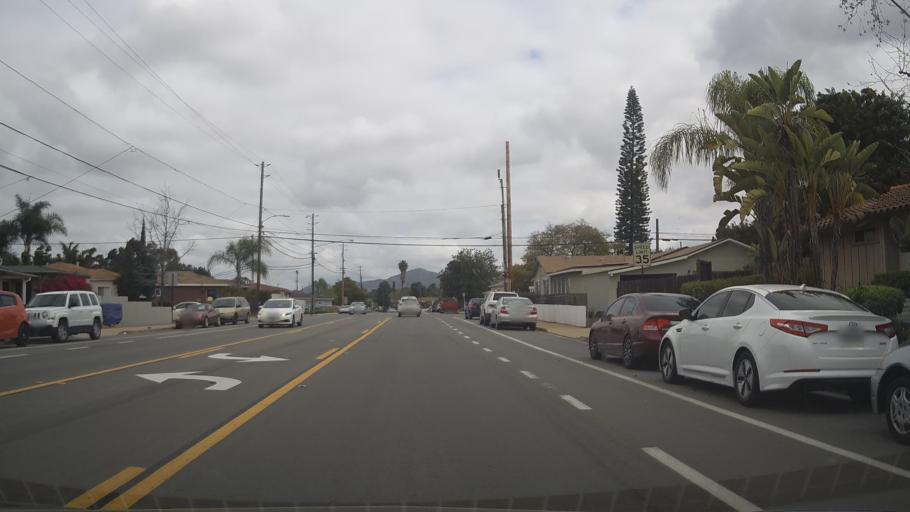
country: US
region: California
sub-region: San Diego County
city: Lemon Grove
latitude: 32.7587
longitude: -117.0474
